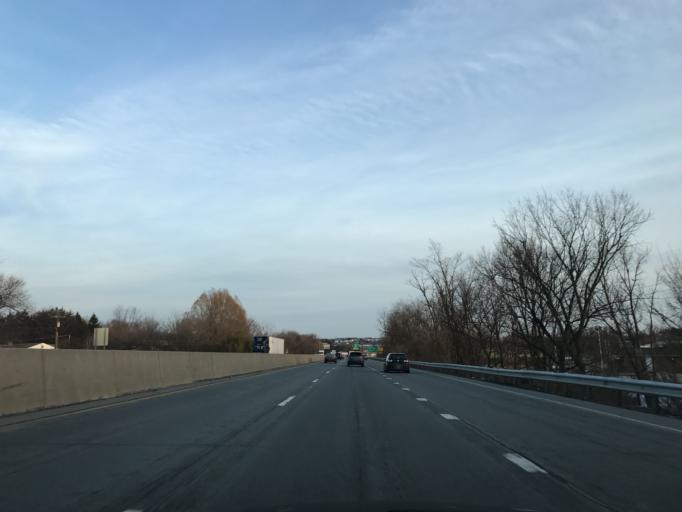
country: US
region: Pennsylvania
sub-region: York County
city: East York
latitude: 39.9690
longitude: -76.6914
